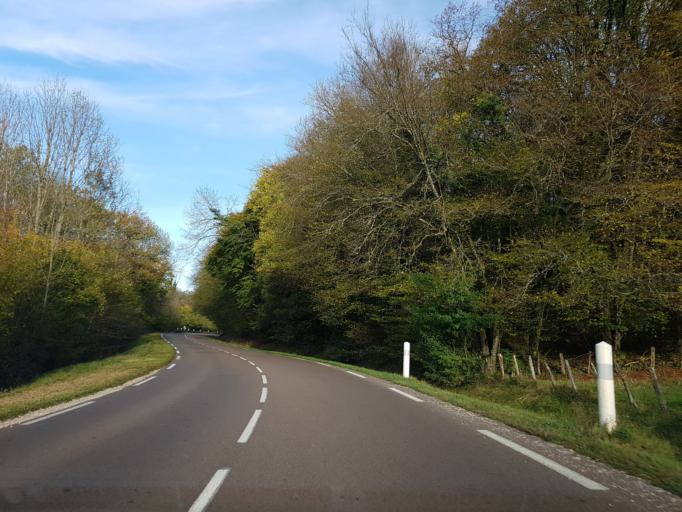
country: FR
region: Bourgogne
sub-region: Departement de la Cote-d'Or
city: Pouilly-en-Auxois
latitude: 47.3038
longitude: 4.6848
